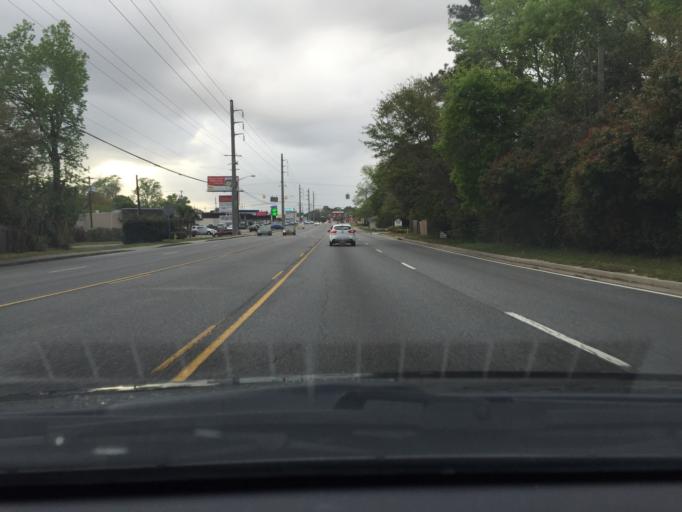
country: US
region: Georgia
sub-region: Chatham County
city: Montgomery
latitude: 31.9970
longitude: -81.1171
